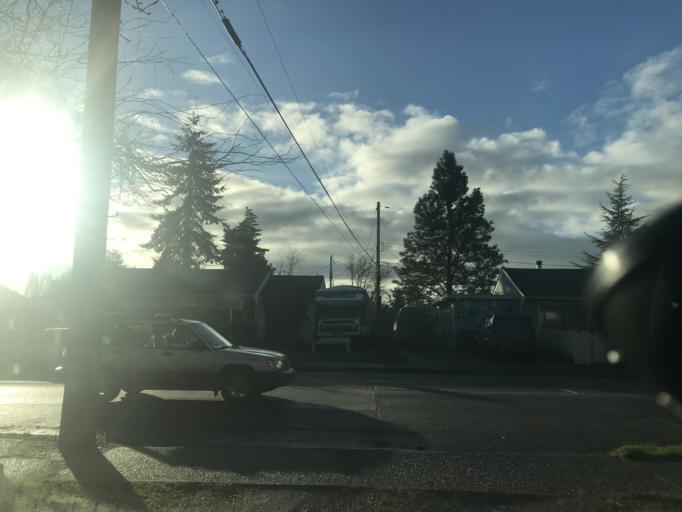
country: US
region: Washington
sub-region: King County
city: White Center
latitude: 47.5212
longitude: -122.3727
